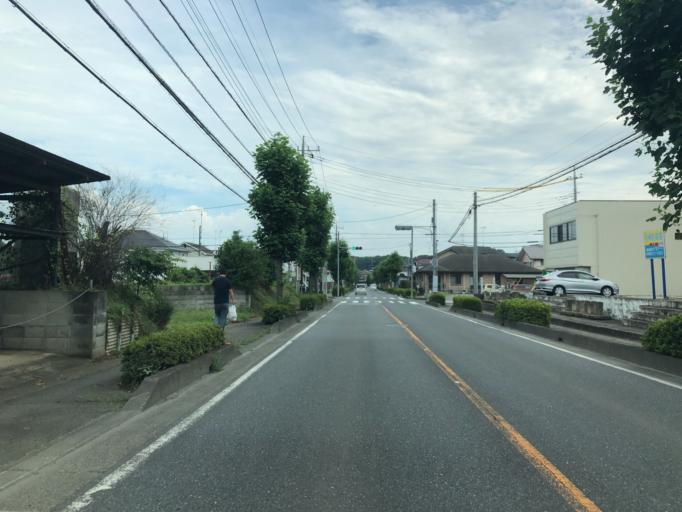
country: JP
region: Saitama
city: Fukiage-fujimi
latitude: 36.0588
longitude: 139.4131
